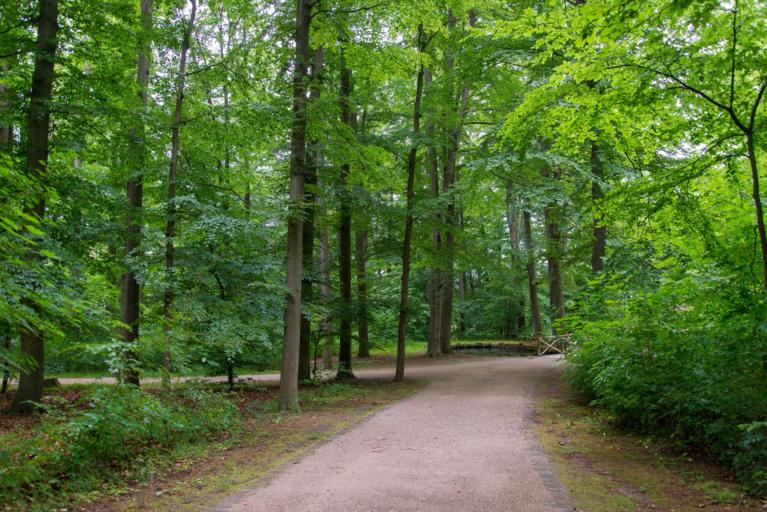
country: DE
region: Bavaria
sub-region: Upper Franconia
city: Bindlach
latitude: 49.9493
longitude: 11.6217
